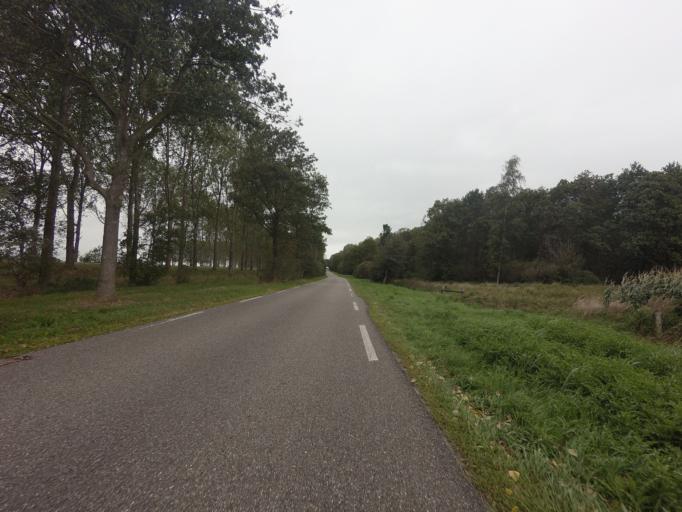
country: NL
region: Friesland
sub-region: Gemeente Opsterland
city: Tijnje
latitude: 53.0200
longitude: 6.0170
